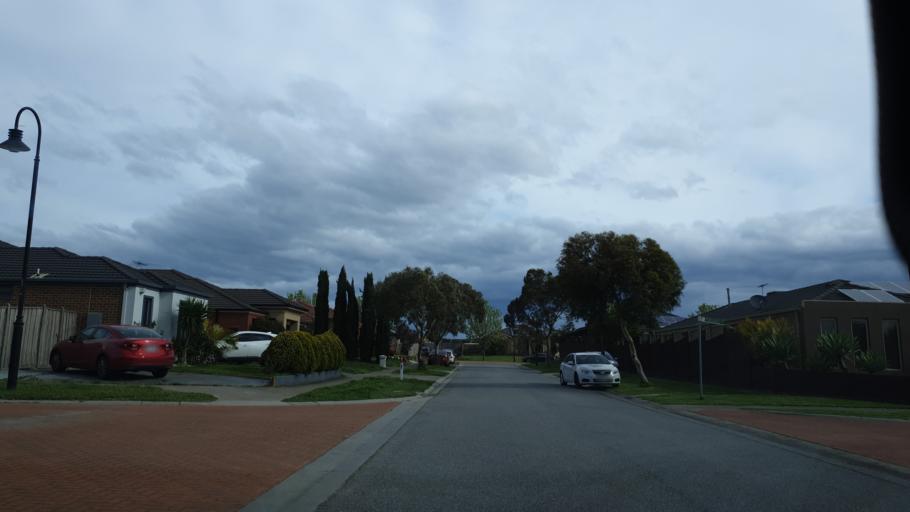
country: AU
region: Victoria
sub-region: Casey
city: Cranbourne North
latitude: -38.0728
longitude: 145.2934
